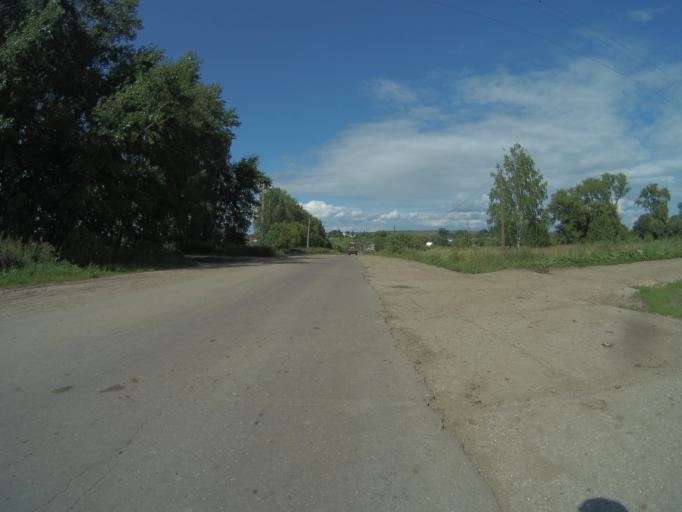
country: RU
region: Vladimir
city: Vladimir
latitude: 56.2612
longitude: 40.3756
